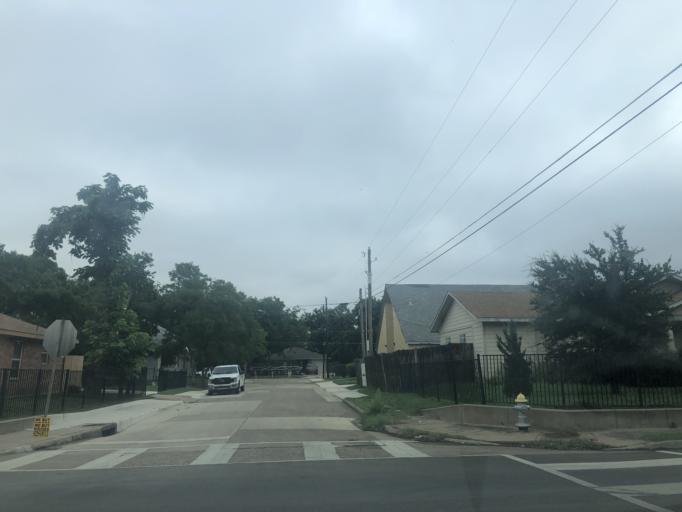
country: US
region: Texas
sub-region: Dallas County
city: Dallas
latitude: 32.7869
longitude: -96.8463
